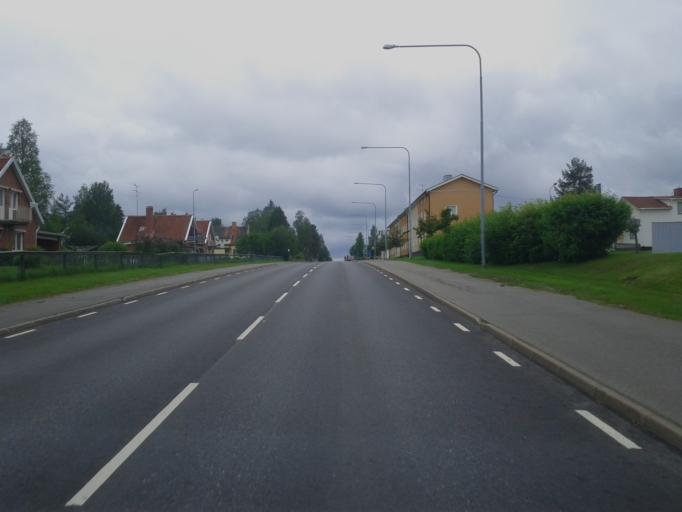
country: SE
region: Vaesterbotten
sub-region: Skelleftea Kommun
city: Boliden
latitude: 64.8685
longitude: 20.3902
